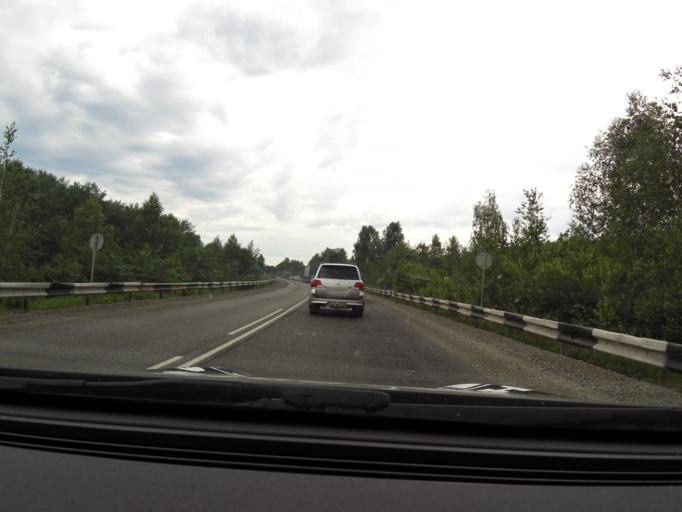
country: RU
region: Chelyabinsk
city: Sim
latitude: 55.0003
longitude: 57.6325
